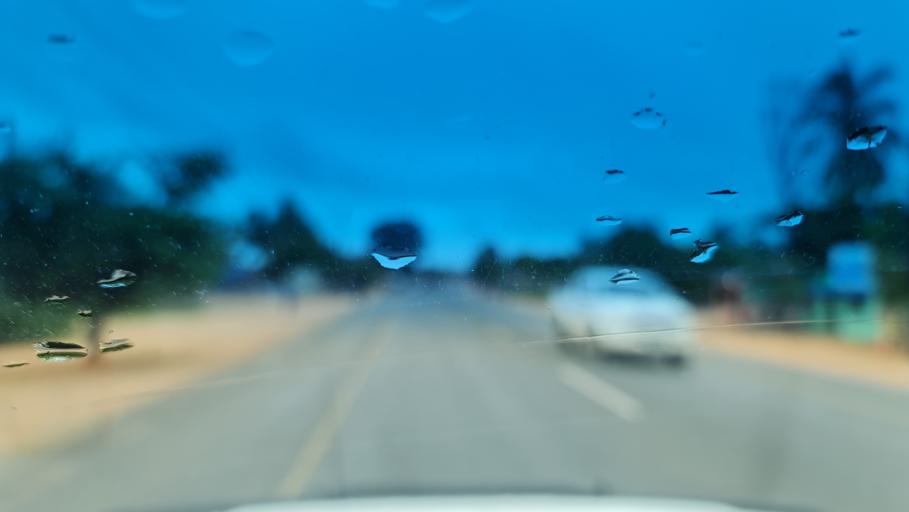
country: MZ
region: Nampula
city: Nampula
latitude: -15.1466
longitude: 39.2982
